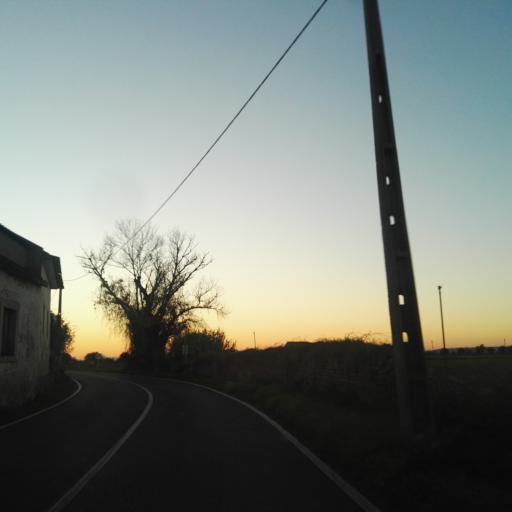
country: PT
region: Santarem
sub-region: Alpiarca
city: Alpiarca
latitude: 39.3073
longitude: -8.5234
